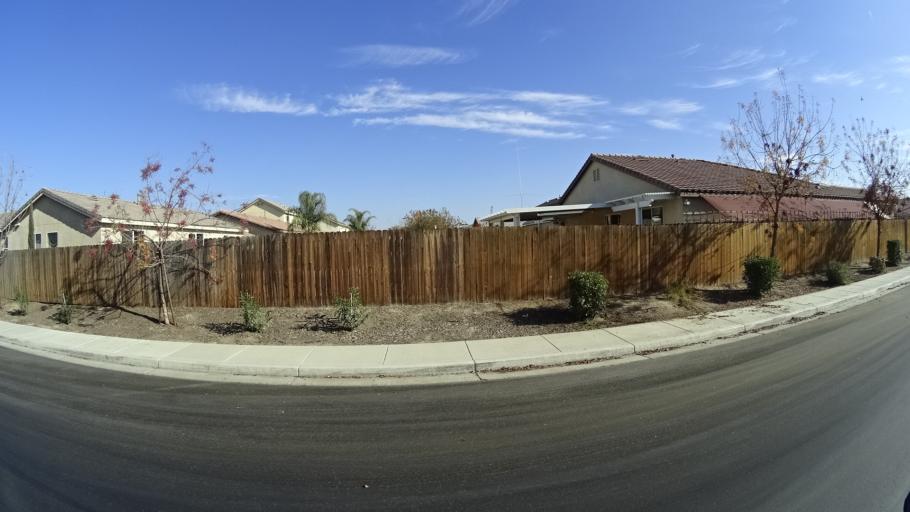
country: US
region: California
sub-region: Kern County
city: Greenfield
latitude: 35.2938
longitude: -119.0648
